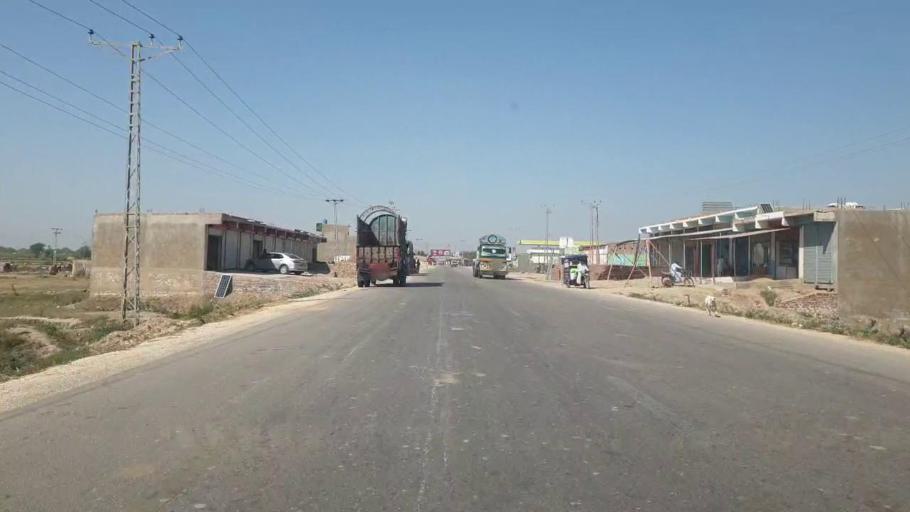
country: PK
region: Sindh
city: Talhar
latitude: 24.8814
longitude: 68.8111
